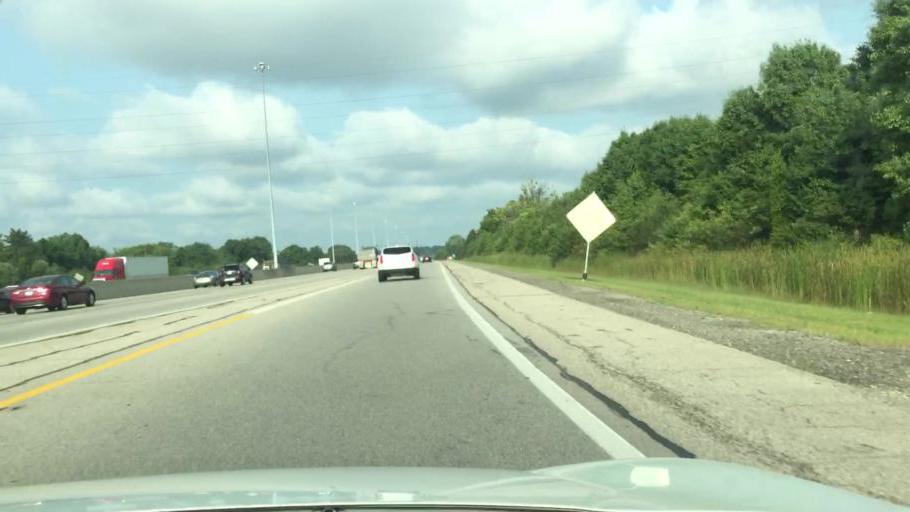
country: US
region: Ohio
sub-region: Franklin County
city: Dublin
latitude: 40.1095
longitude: -83.0957
